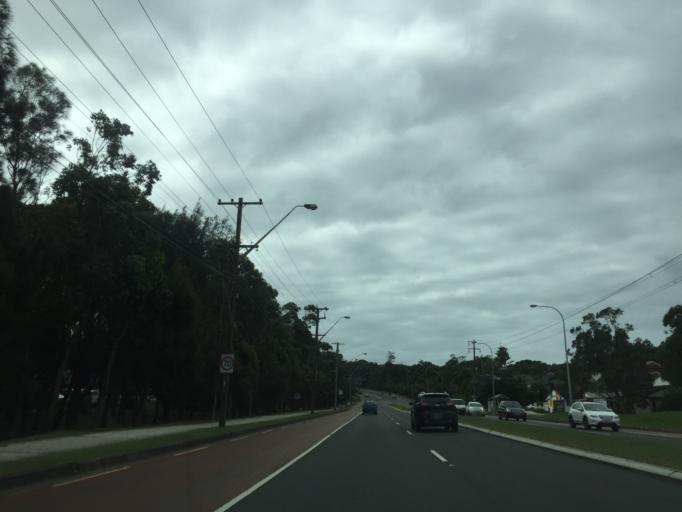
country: AU
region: New South Wales
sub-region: Pittwater
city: Warriewood
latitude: -33.6946
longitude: 151.3029
